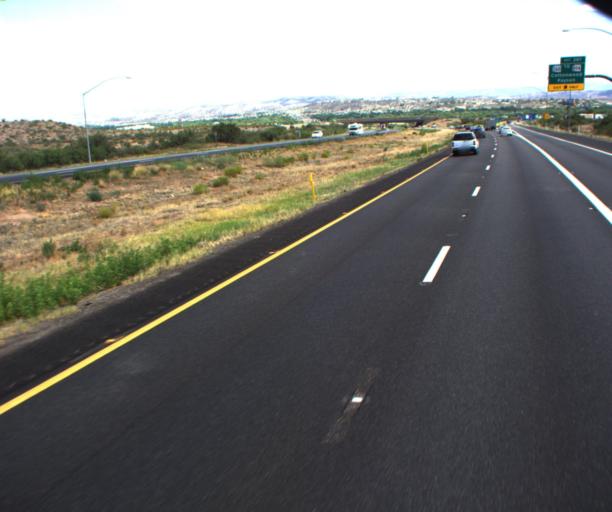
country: US
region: Arizona
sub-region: Yavapai County
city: Camp Verde
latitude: 34.5730
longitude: -111.8881
